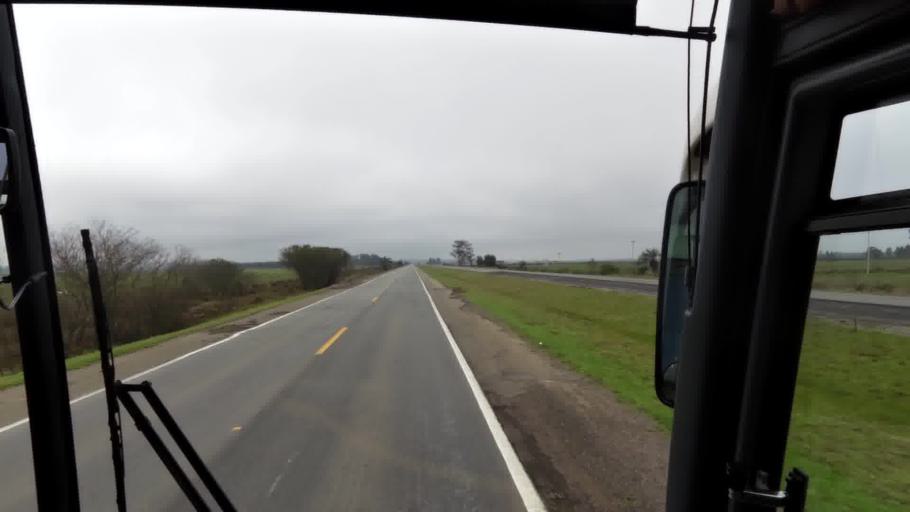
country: BR
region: Rio Grande do Sul
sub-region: Pelotas
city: Pelotas
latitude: -31.5924
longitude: -52.2840
